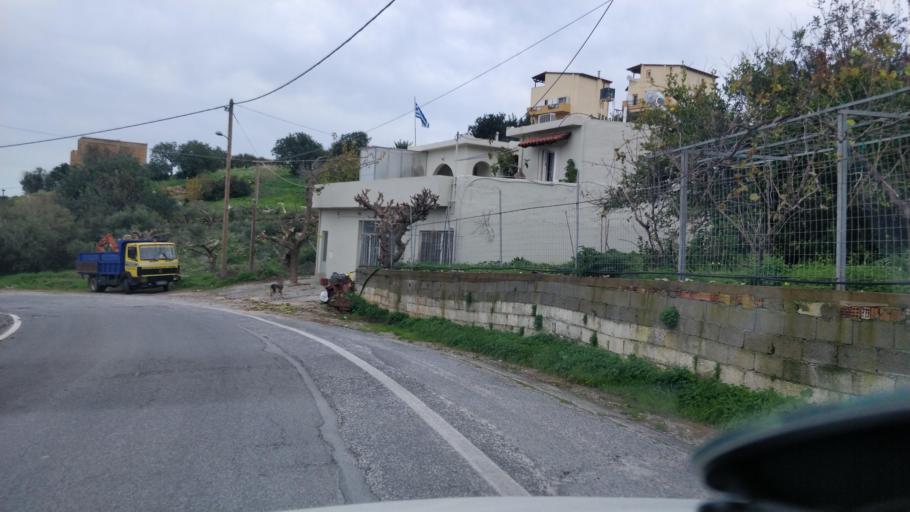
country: GR
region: Crete
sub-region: Nomos Lasithiou
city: Agios Nikolaos
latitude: 35.1149
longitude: 25.7261
